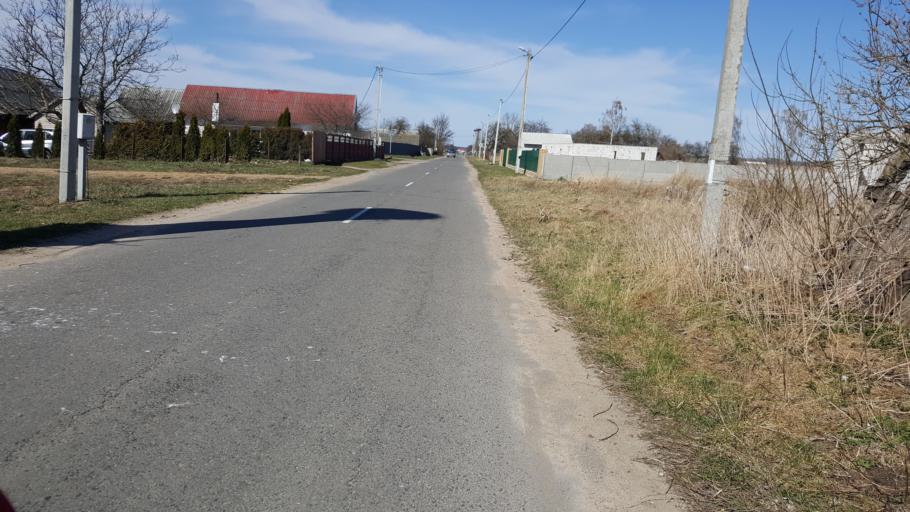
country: BY
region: Brest
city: Charnawchytsy
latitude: 52.3065
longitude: 23.7796
